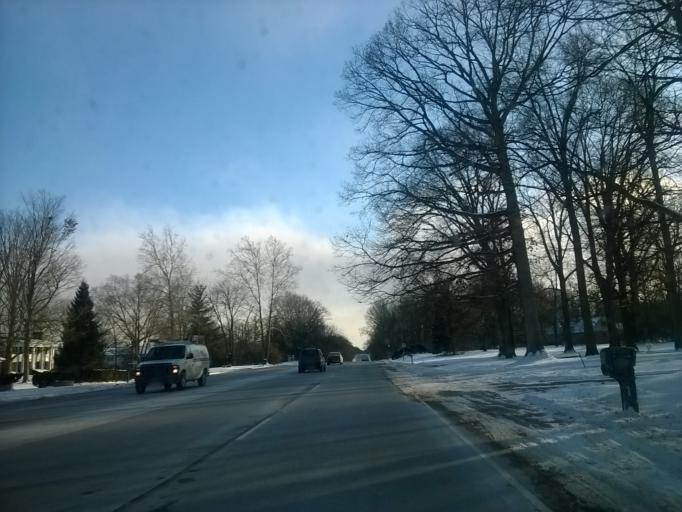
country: US
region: Indiana
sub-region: Marion County
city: Meridian Hills
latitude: 39.9030
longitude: -86.1580
